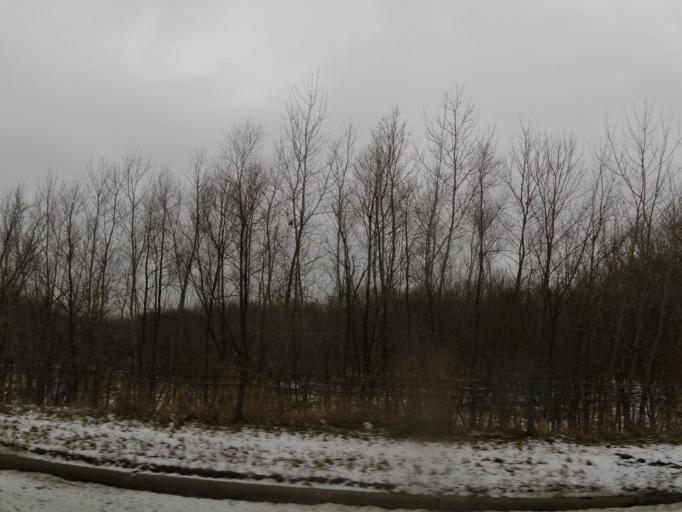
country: US
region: Minnesota
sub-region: Wright County
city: Delano
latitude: 45.0461
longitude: -93.7965
